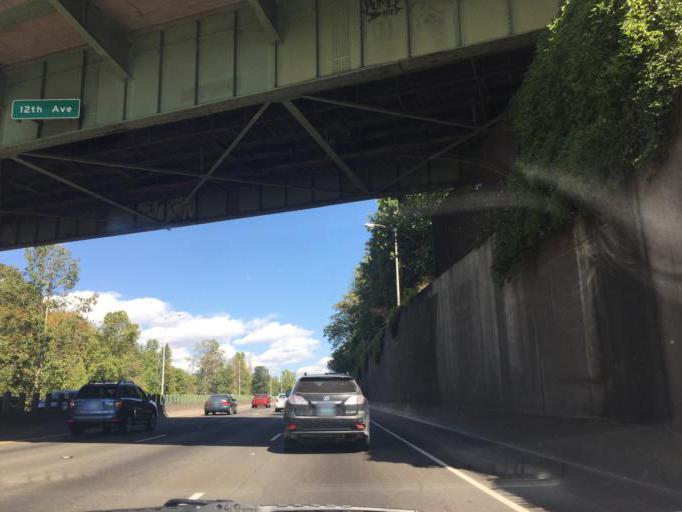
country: US
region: Oregon
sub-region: Multnomah County
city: Portland
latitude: 45.5283
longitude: -122.6539
